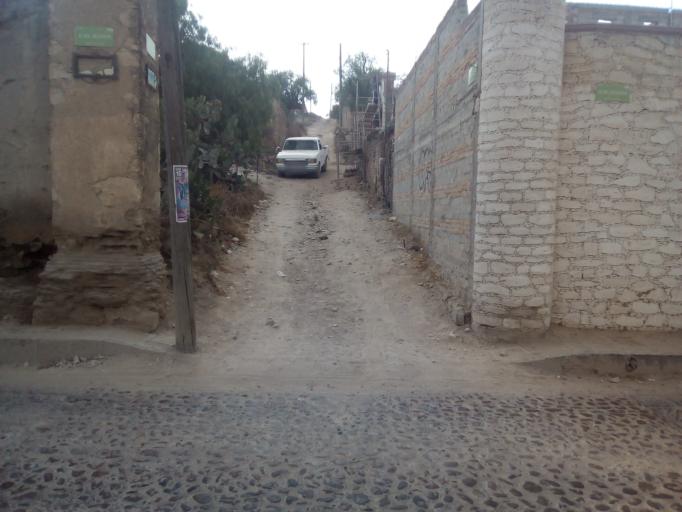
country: MX
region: Guanajuato
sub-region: San Luis de la Paz
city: San Ignacio
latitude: 21.2255
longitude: -100.4930
